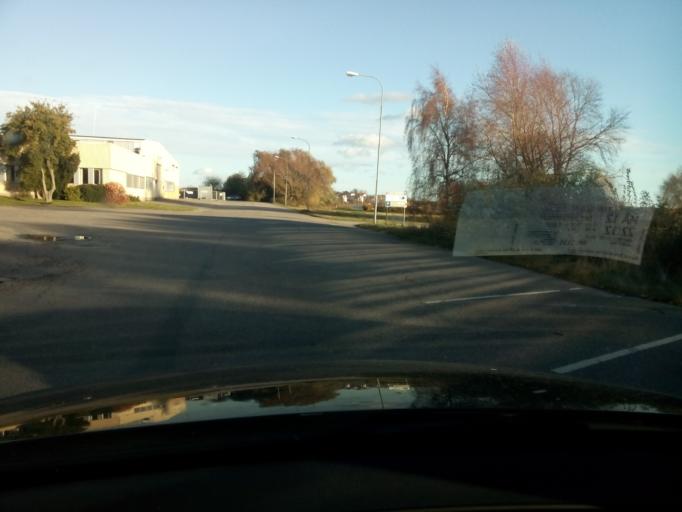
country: SE
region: Soedermanland
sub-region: Nykopings Kommun
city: Nykoping
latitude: 58.7454
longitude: 17.0250
